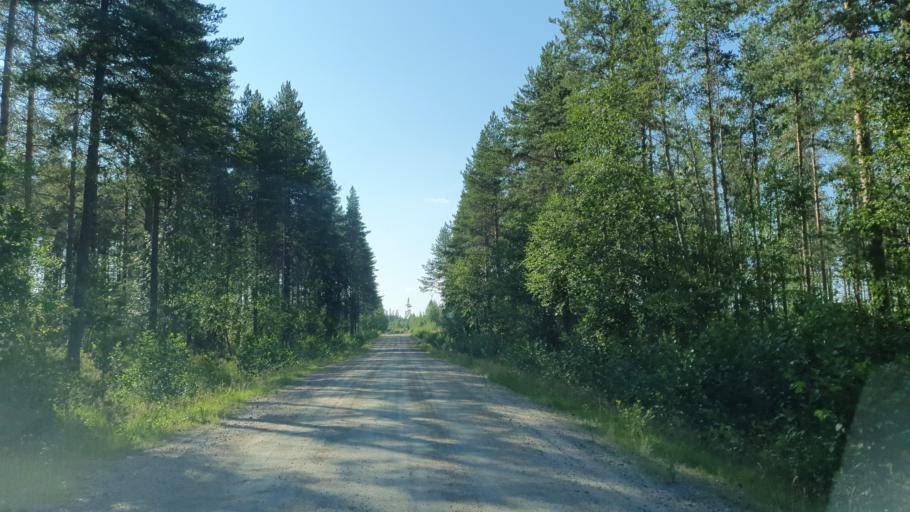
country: FI
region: Kainuu
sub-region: Kehys-Kainuu
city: Kuhmo
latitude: 64.0297
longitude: 29.6967
